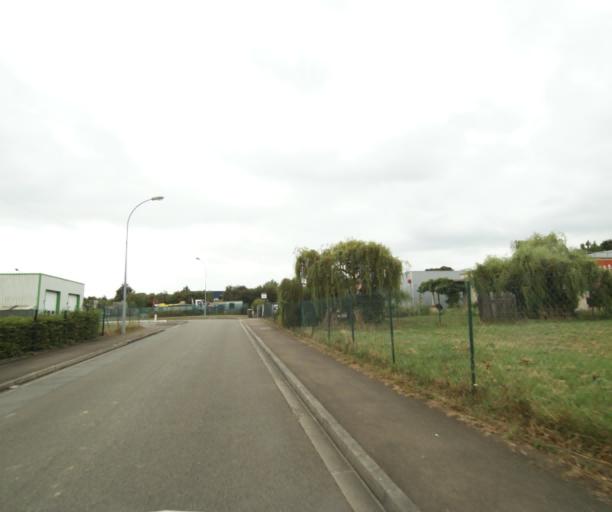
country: FR
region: Pays de la Loire
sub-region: Departement de la Sarthe
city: Solesmes
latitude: 47.8364
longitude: -0.3052
